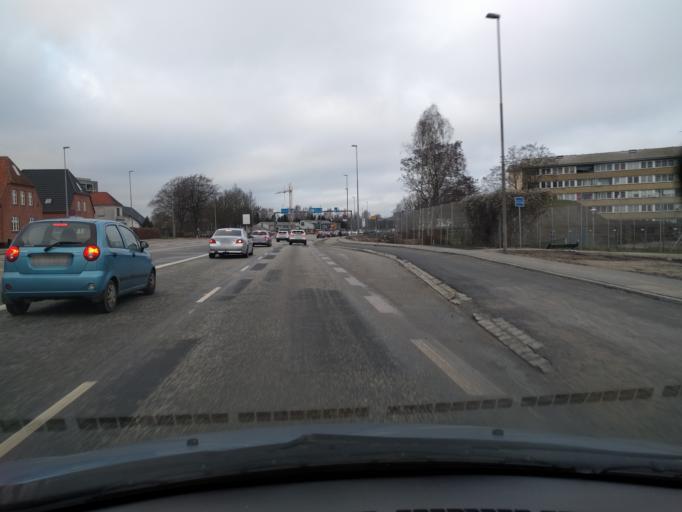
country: DK
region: South Denmark
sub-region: Odense Kommune
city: Odense
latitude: 55.3914
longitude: 10.4230
